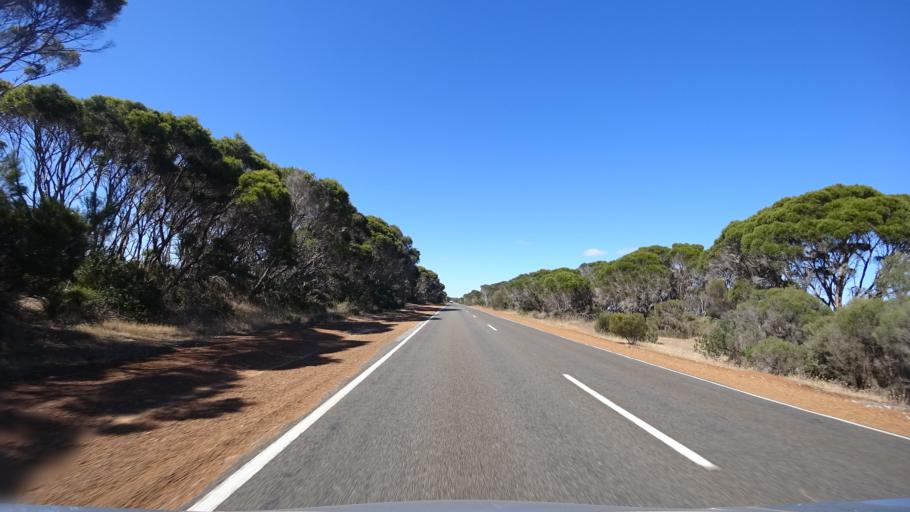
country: AU
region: South Australia
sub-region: Kangaroo Island
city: Kingscote
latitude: -35.7111
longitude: 137.5637
